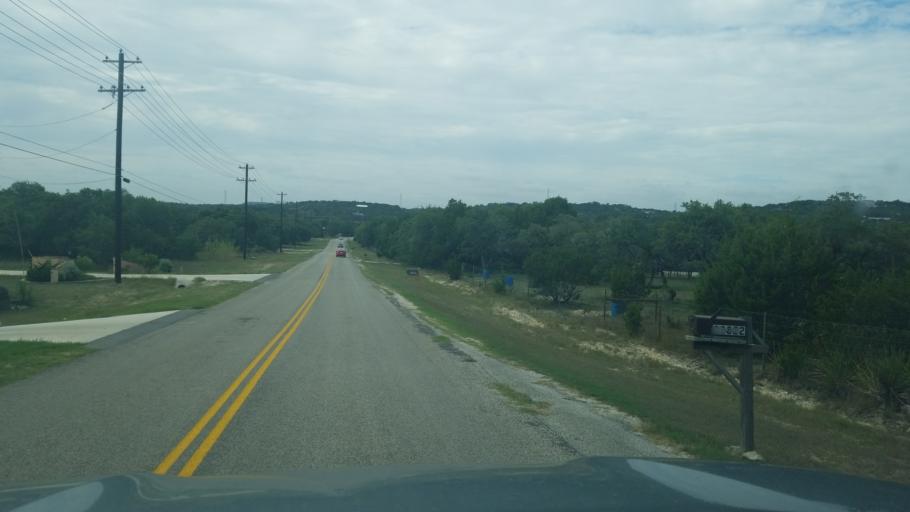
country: US
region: Texas
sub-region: Comal County
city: Bulverde
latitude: 29.7921
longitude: -98.4110
